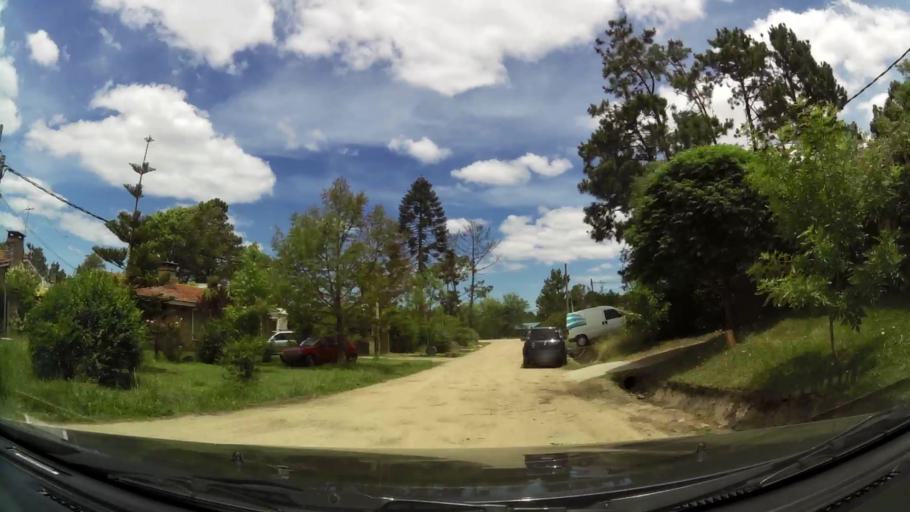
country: UY
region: Canelones
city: Empalme Olmos
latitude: -34.7966
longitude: -55.8892
